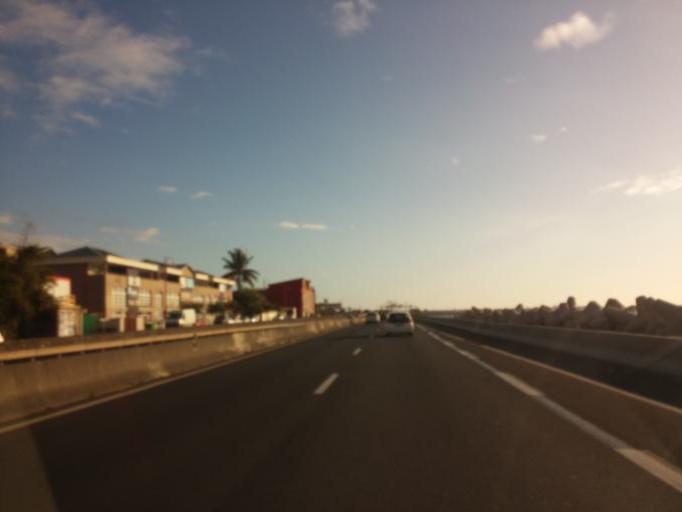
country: RE
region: Reunion
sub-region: Reunion
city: La Possession
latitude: -20.9241
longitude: 55.3410
